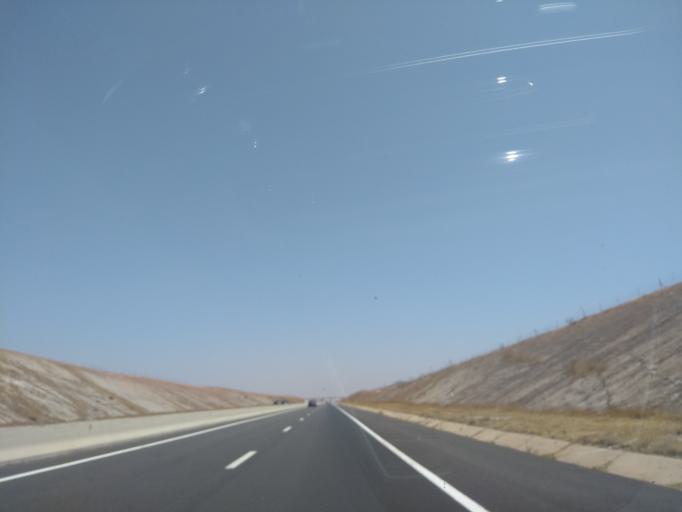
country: MA
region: Marrakech-Tensift-Al Haouz
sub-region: Kelaa-Des-Sraghna
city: Sidi Abdallah
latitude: 32.3111
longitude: -7.9589
